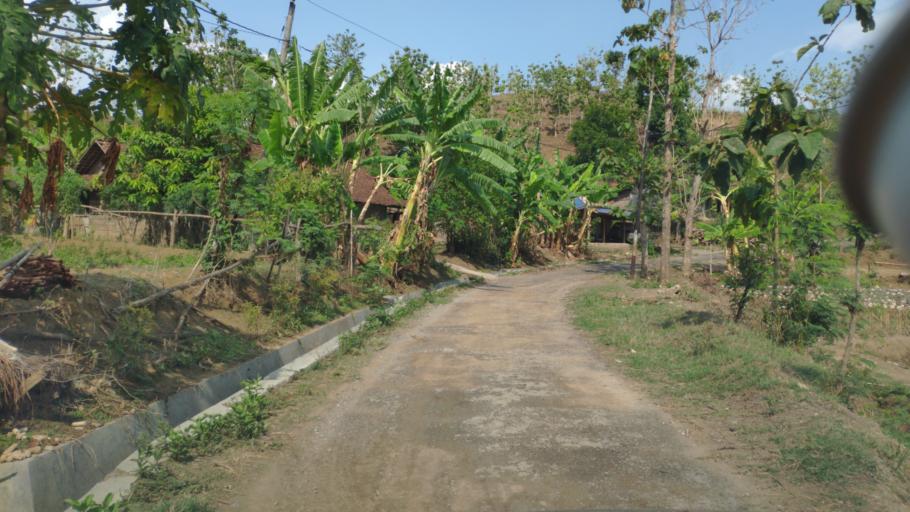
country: ID
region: Central Java
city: Semanggi
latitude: -7.0587
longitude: 111.4302
